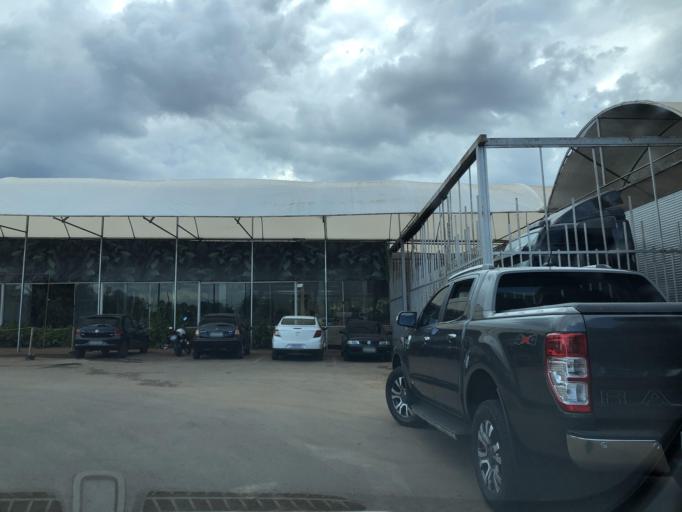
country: BR
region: Federal District
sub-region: Brasilia
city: Brasilia
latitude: -15.8136
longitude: -48.0091
